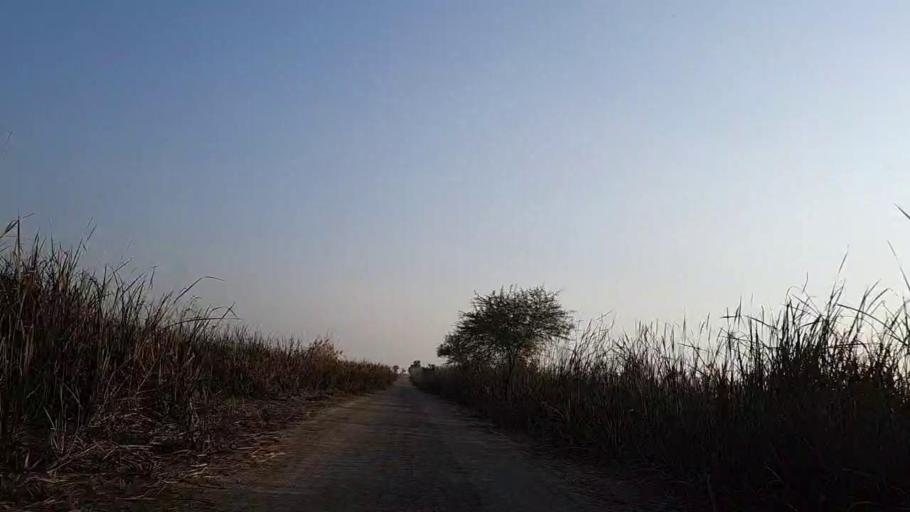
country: PK
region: Sindh
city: Sakrand
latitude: 26.0265
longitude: 68.4382
